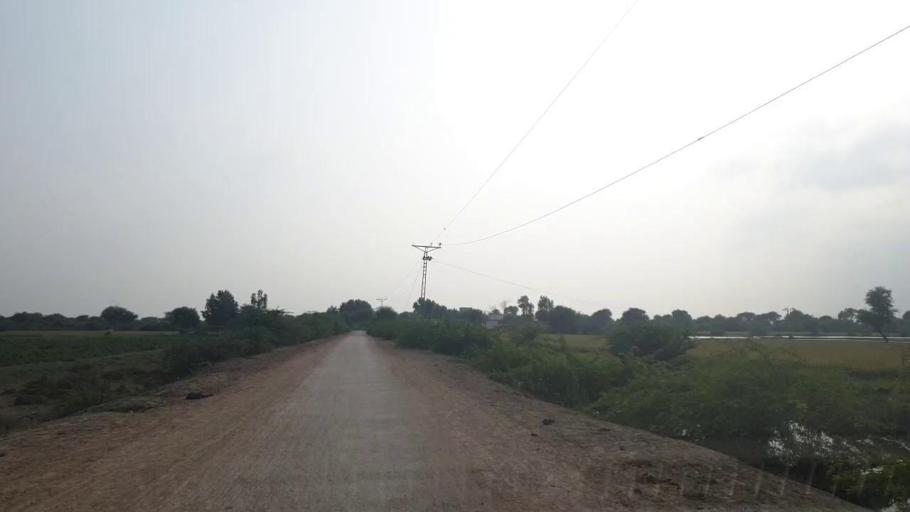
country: PK
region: Sindh
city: Badin
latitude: 24.6134
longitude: 68.6858
